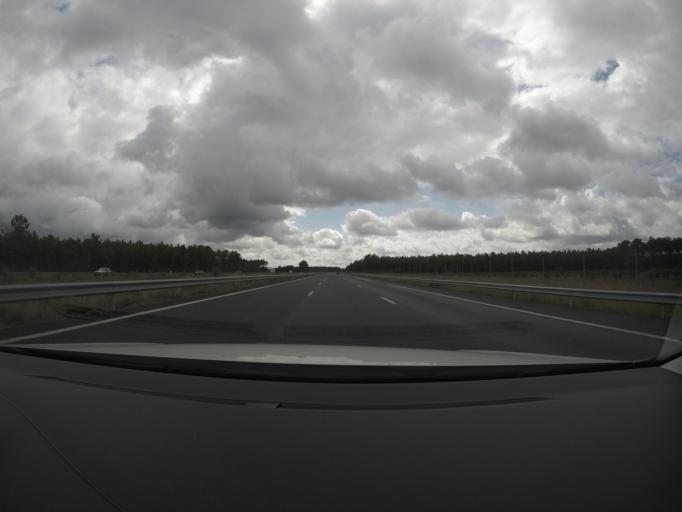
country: FR
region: Aquitaine
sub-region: Departement de la Gironde
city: Belin-Beliet
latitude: 44.4665
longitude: -0.8194
